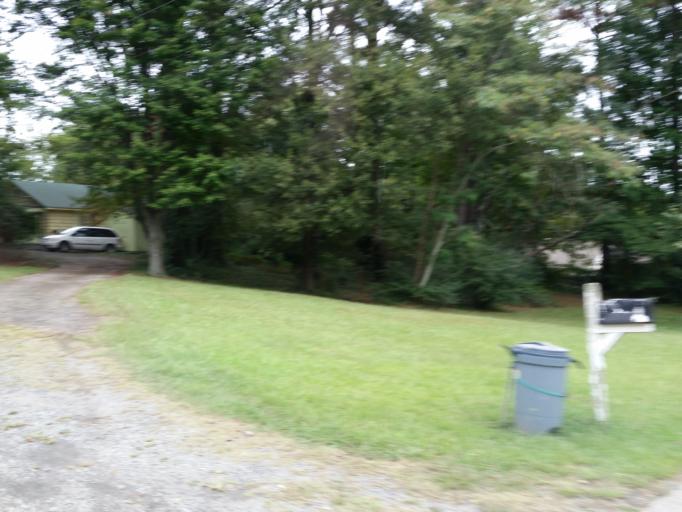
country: US
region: Georgia
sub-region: Cobb County
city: Marietta
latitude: 33.9542
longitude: -84.5309
